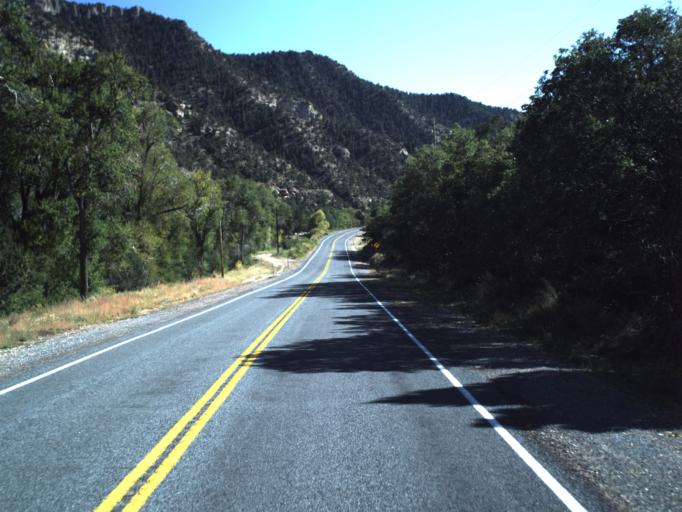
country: US
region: Utah
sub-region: Iron County
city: Parowan
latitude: 37.8170
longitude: -112.8091
